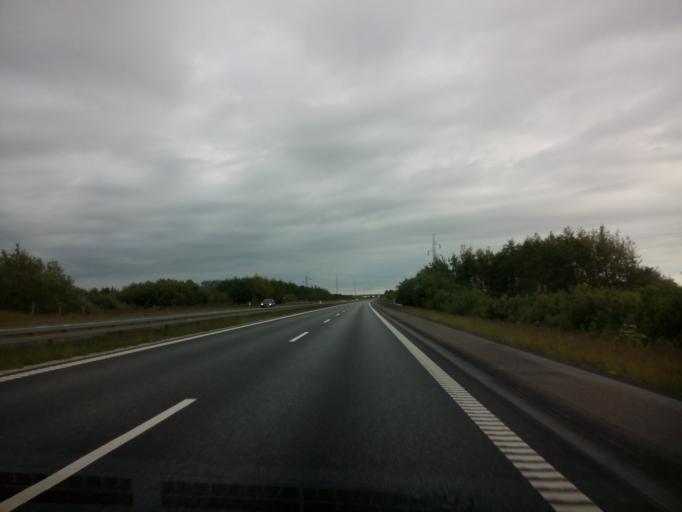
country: DK
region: North Denmark
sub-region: Hjorring Kommune
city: Vra
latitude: 57.3428
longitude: 10.0294
